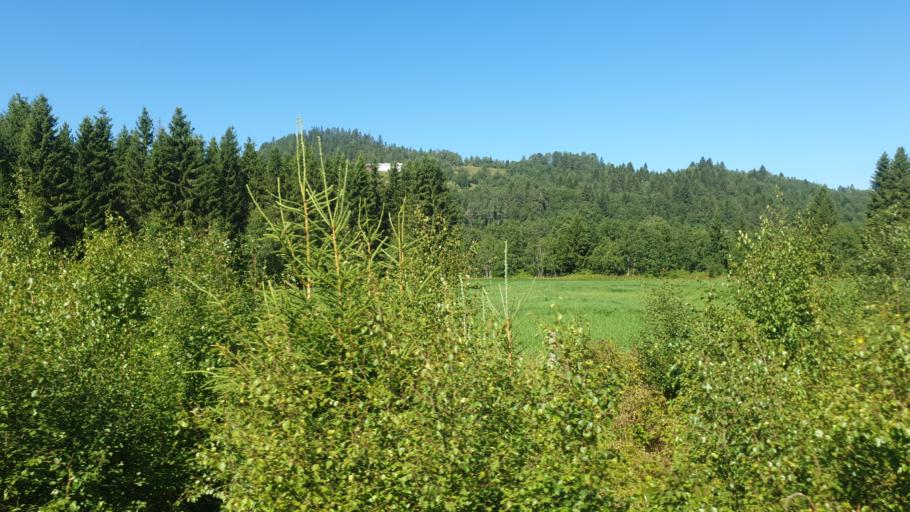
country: NO
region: Sor-Trondelag
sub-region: Meldal
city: Meldal
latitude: 63.1790
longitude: 9.7612
